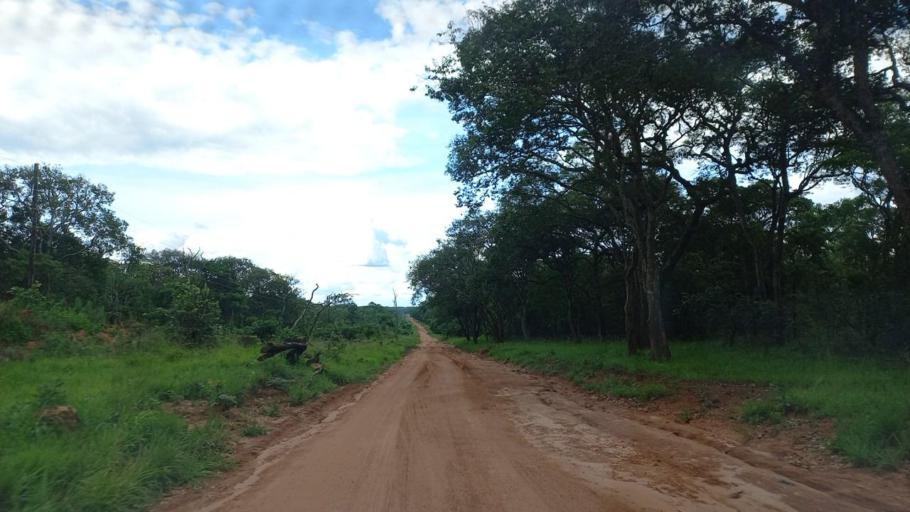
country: ZM
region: North-Western
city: Mwinilunga
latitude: -11.8119
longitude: 24.3675
